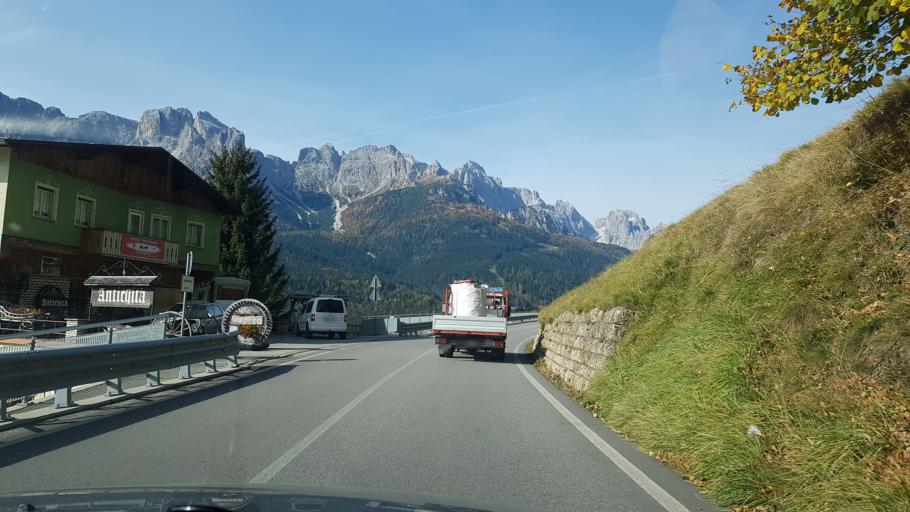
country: IT
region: Veneto
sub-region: Provincia di Belluno
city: Candide
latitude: 46.5924
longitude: 12.5057
